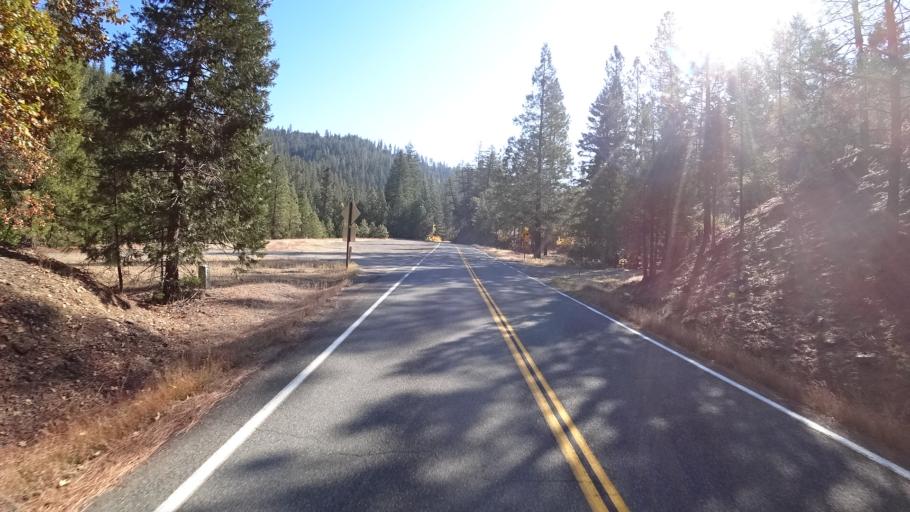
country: US
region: California
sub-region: Siskiyou County
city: Happy Camp
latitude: 41.7636
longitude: -123.0196
